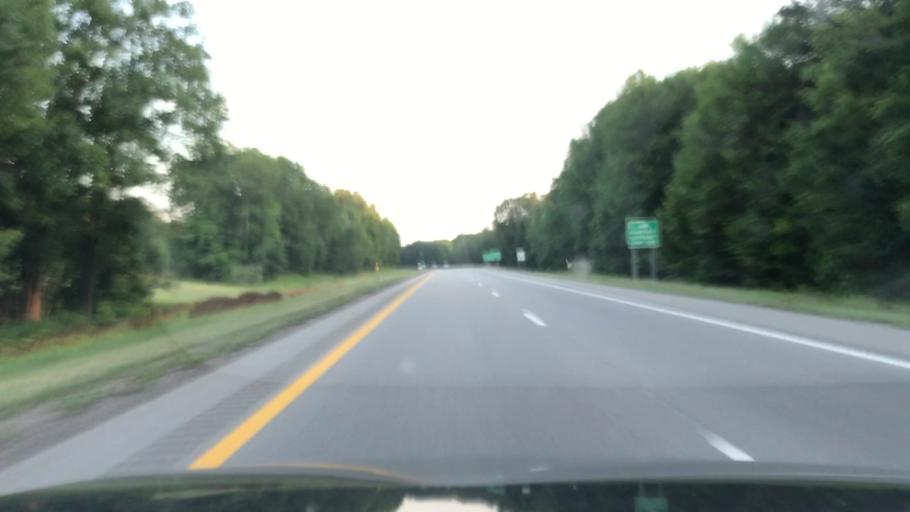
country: US
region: Michigan
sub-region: Montcalm County
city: Howard City
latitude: 43.4994
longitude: -85.4867
